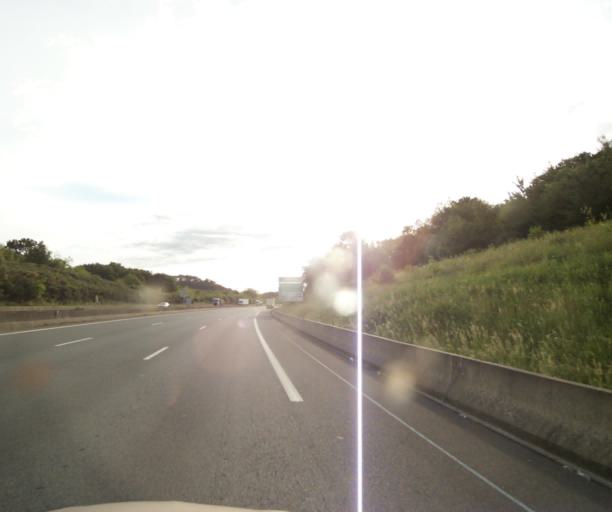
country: FR
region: Aquitaine
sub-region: Departement des Pyrenees-Atlantiques
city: Anglet
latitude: 43.4605
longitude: -1.5175
